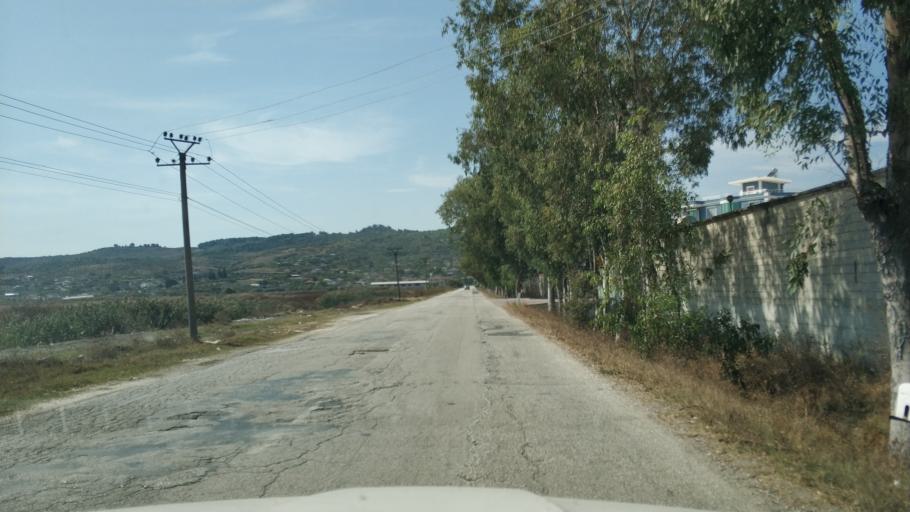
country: AL
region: Fier
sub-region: Rrethi i Lushnjes
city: Kolonje
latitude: 40.8290
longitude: 19.6173
